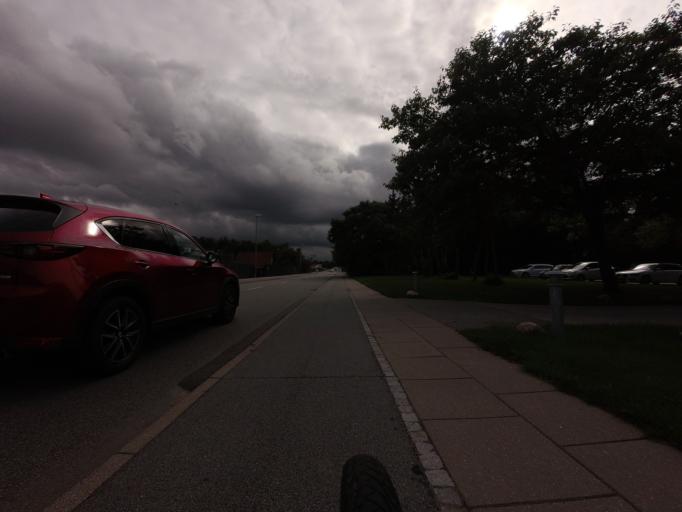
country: DK
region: North Denmark
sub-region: Hjorring Kommune
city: Hjorring
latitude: 57.4761
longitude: 9.9910
